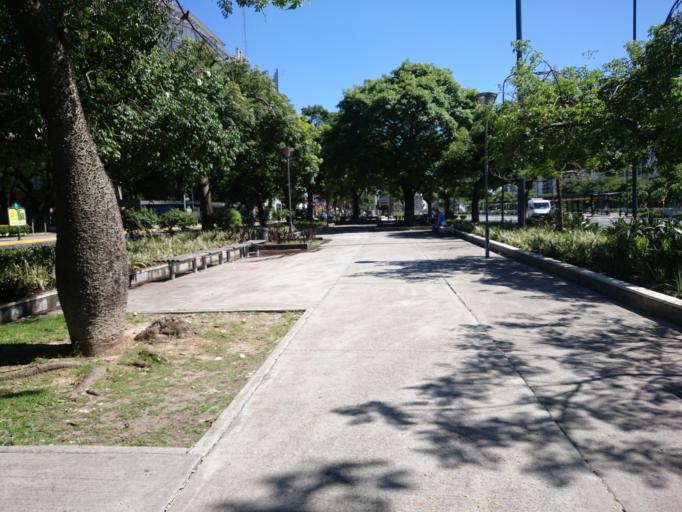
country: AR
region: Buenos Aires F.D.
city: Retiro
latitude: -34.5975
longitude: -58.3823
